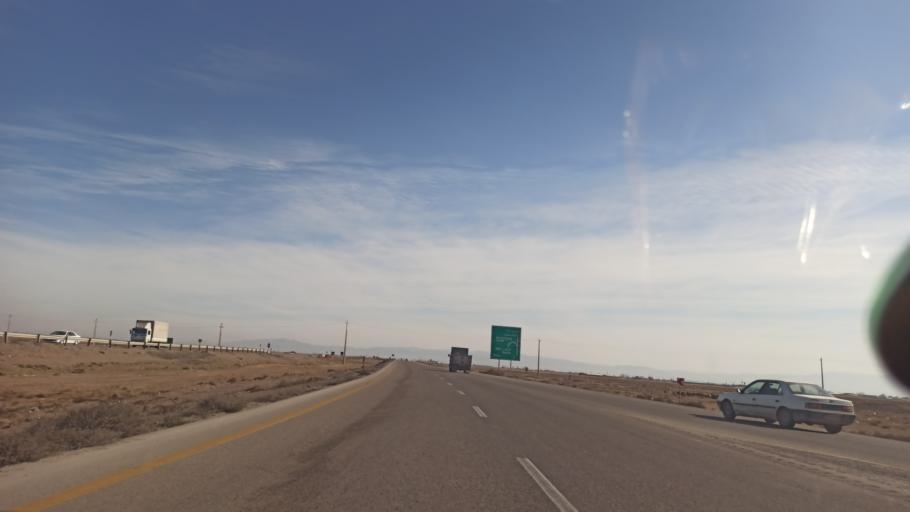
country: IR
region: Qazvin
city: Bu'in Zahra
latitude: 35.8401
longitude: 50.0631
